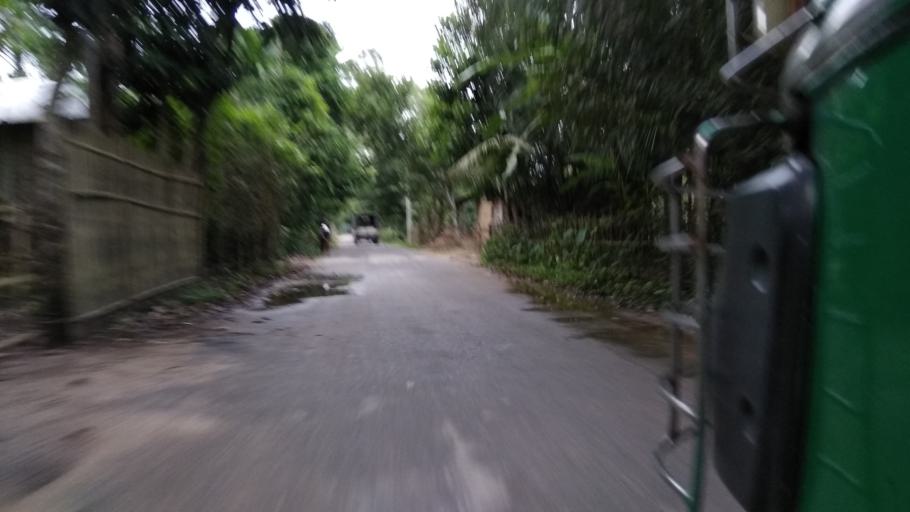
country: IN
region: Tripura
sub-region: Dhalai
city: Kamalpur
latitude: 24.2151
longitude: 91.8554
